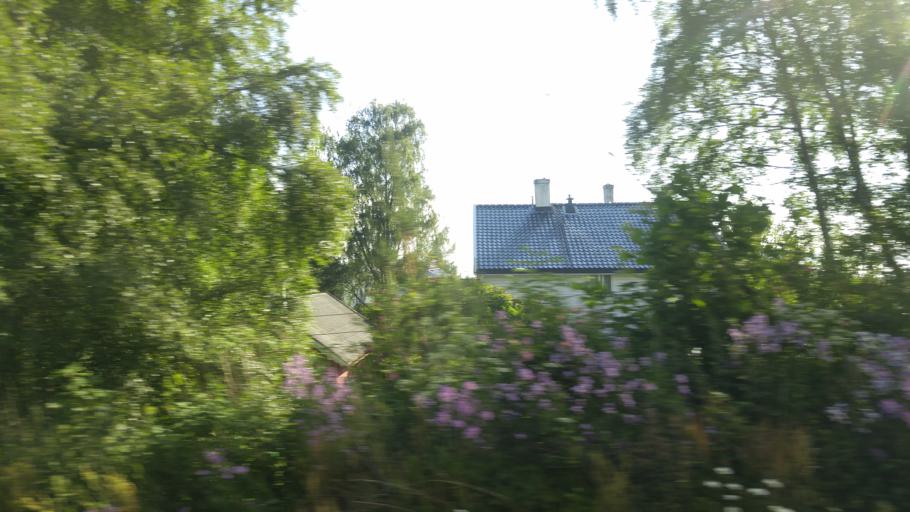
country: NO
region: Sor-Trondelag
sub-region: Trondheim
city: Trondheim
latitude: 63.4348
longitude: 10.4938
